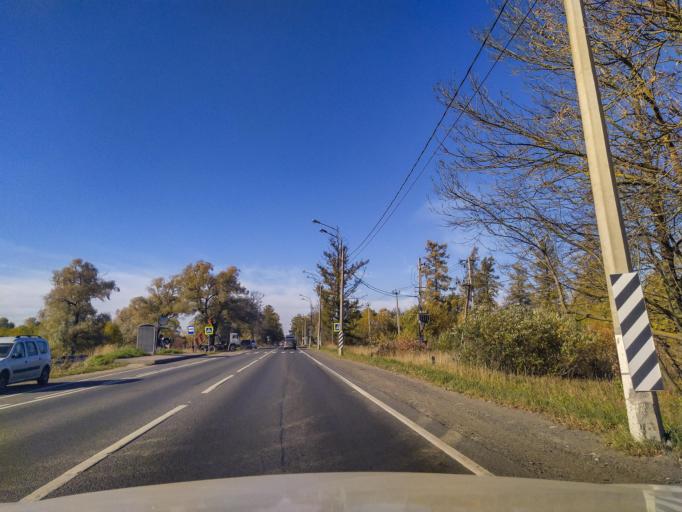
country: RU
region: St.-Petersburg
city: Aleksandrovskaya
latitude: 59.7045
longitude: 30.3455
